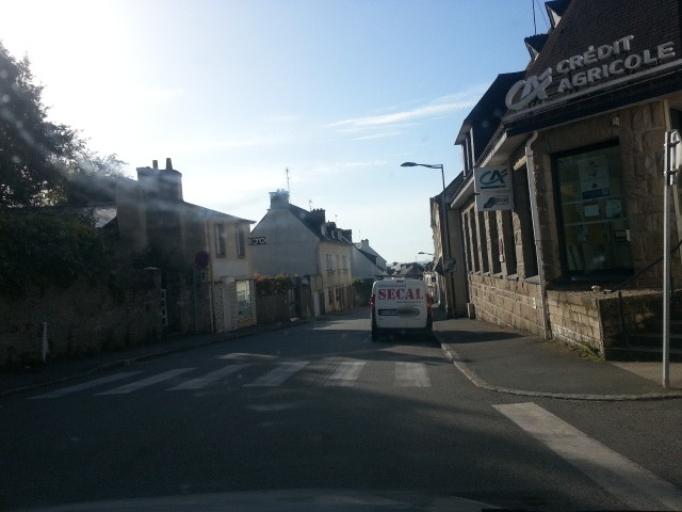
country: FR
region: Brittany
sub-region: Departement du Morbihan
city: Le Faouet
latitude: 48.0321
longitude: -3.4888
